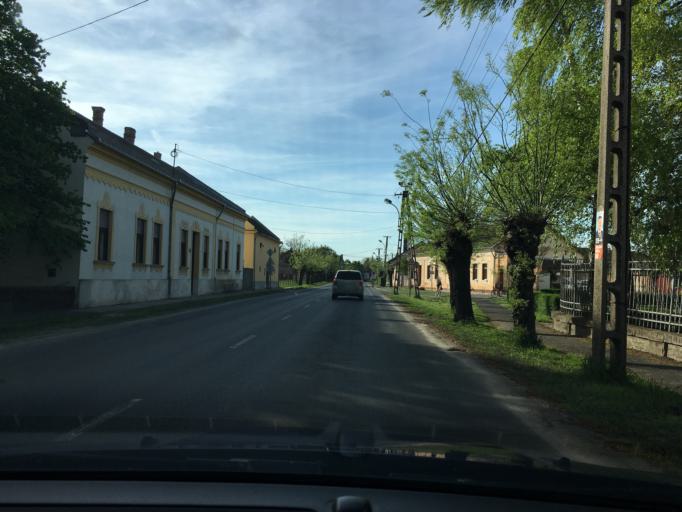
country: HU
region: Bekes
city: Mezobereny
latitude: 46.8287
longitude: 21.0291
